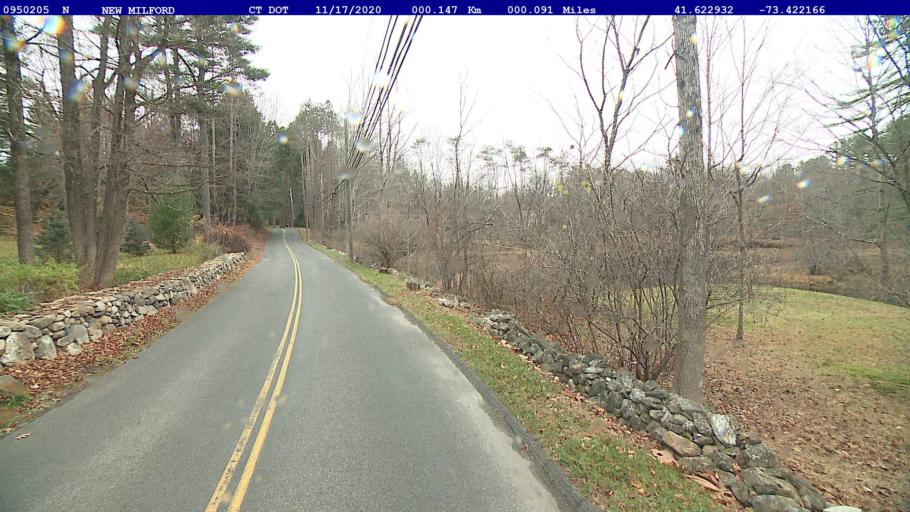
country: US
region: Connecticut
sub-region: Litchfield County
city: New Milford
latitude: 41.6229
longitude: -73.4222
